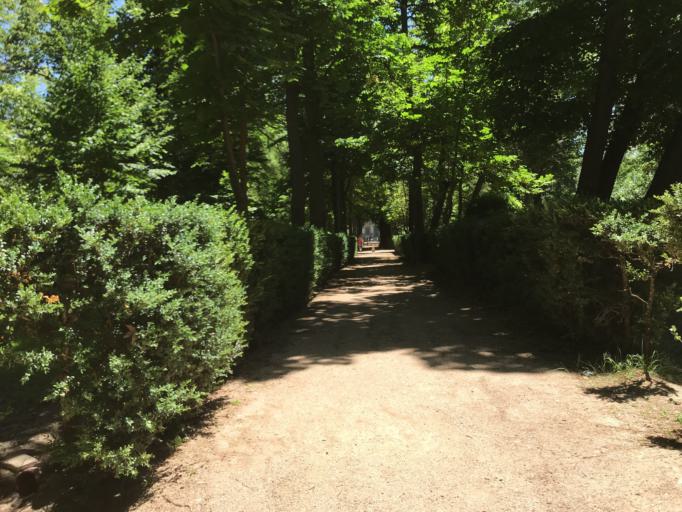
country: ES
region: Madrid
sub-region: Provincia de Madrid
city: Aranjuez
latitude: 40.0382
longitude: -3.6103
